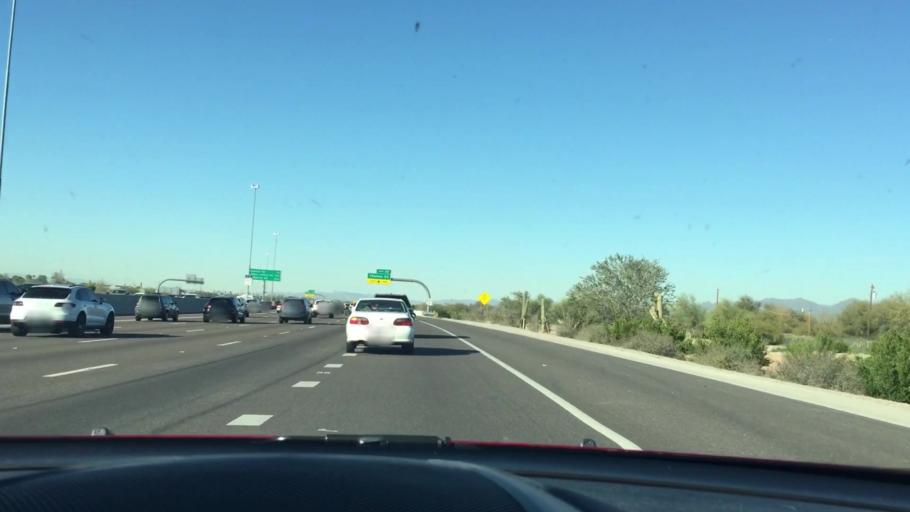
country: US
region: Arizona
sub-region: Maricopa County
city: Scottsdale
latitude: 33.4715
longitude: -111.8928
